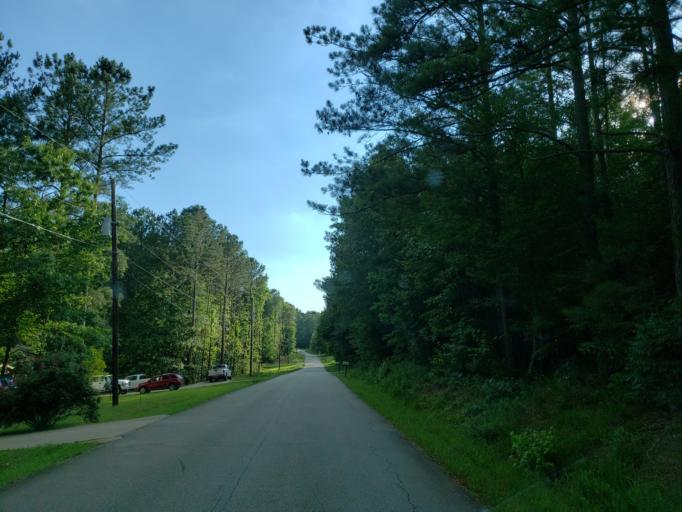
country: US
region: Georgia
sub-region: Haralson County
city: Buchanan
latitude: 33.9047
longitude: -85.2498
